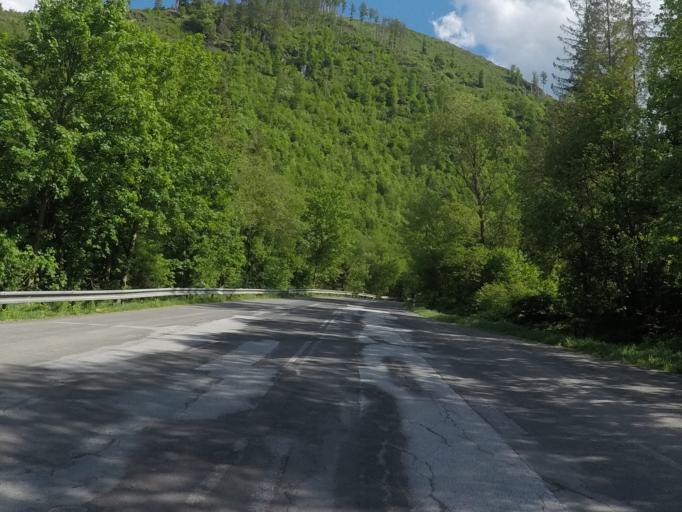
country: SK
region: Presovsky
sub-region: Okres Poprad
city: Poprad
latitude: 48.9541
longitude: 20.2947
